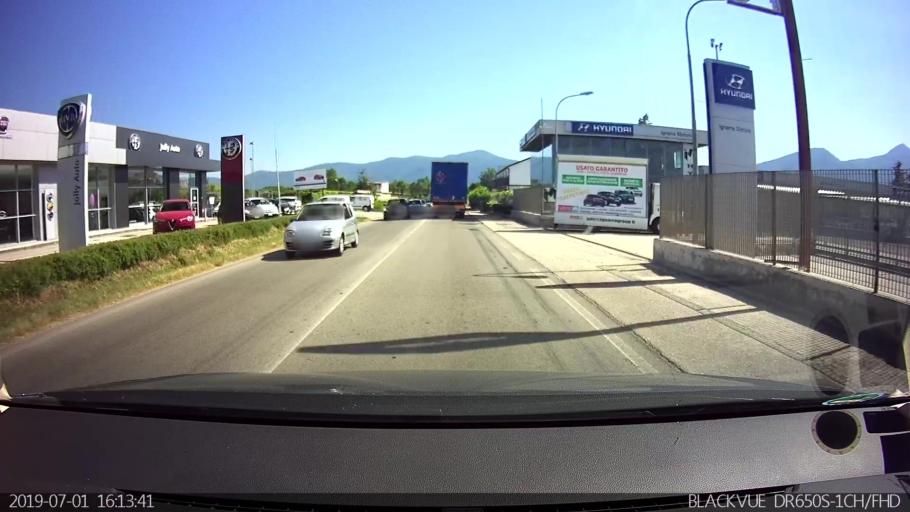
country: IT
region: Latium
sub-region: Provincia di Frosinone
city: Ceccano
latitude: 41.6057
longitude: 13.3004
